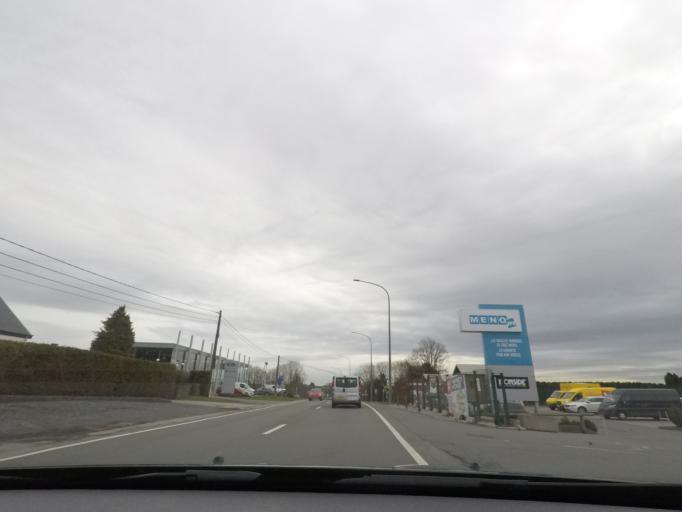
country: BE
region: Wallonia
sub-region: Province du Luxembourg
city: Bastogne
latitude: 49.9944
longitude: 5.7279
